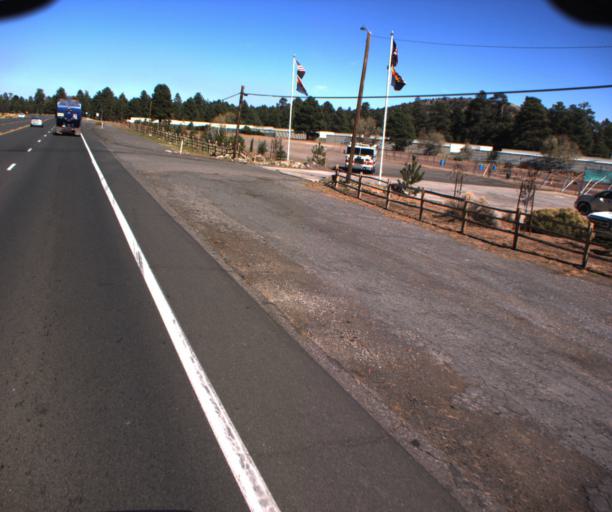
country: US
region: Arizona
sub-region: Coconino County
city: Flagstaff
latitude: 35.2704
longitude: -111.5450
